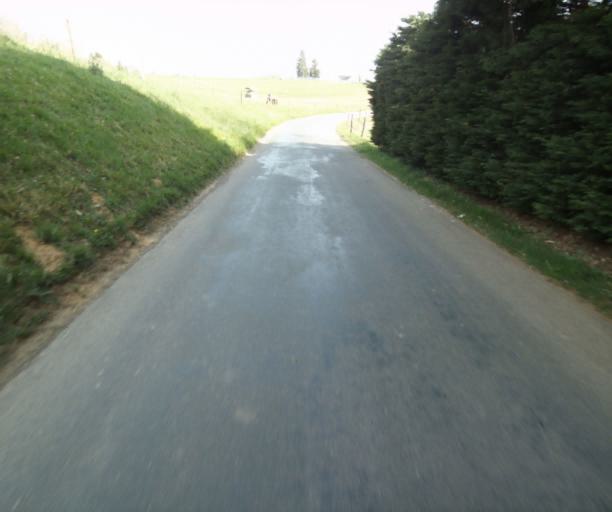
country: FR
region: Limousin
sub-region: Departement de la Correze
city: Naves
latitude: 45.3311
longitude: 1.7529
